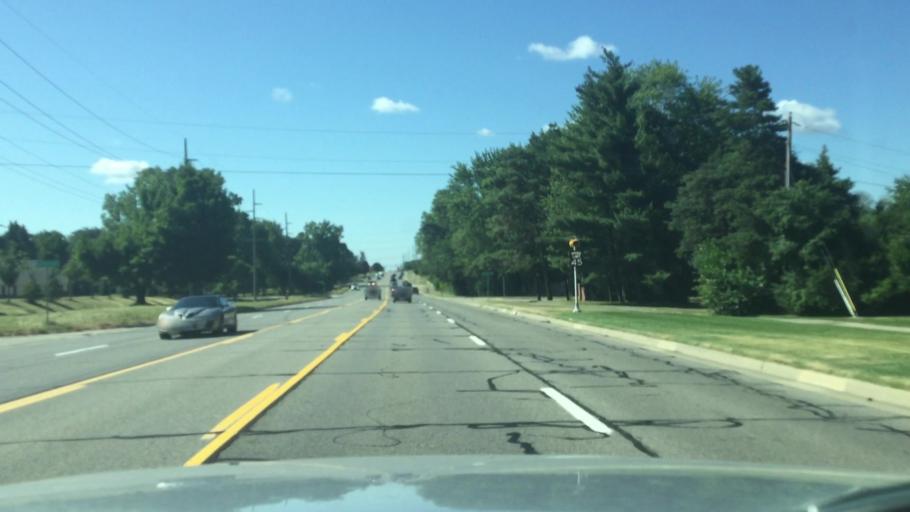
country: US
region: Michigan
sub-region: Oakland County
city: West Bloomfield Township
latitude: 42.5537
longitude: -83.3612
